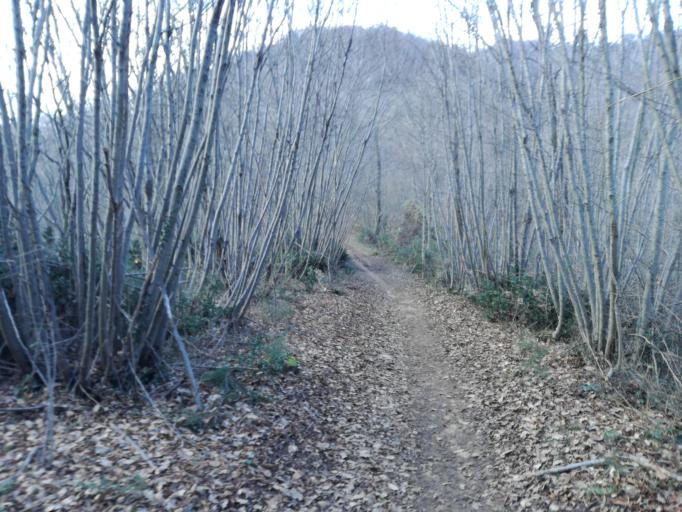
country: IT
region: Veneto
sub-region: Provincia di Padova
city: Galzignano
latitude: 45.2980
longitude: 11.7155
